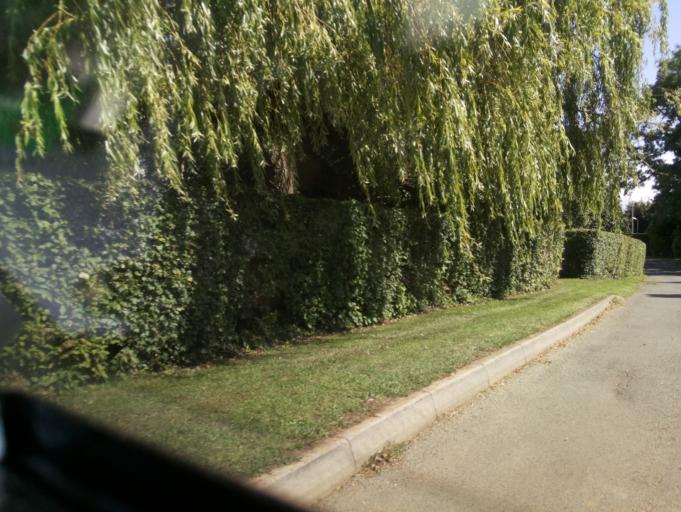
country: GB
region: England
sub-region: Milton Keynes
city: Calverton
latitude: 52.0023
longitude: -0.8629
